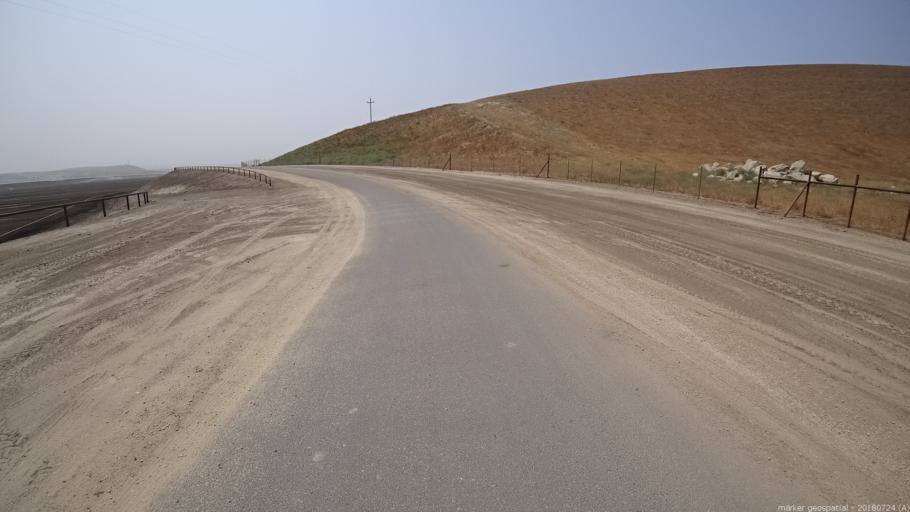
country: US
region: California
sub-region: Monterey County
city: King City
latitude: 36.1900
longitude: -121.0442
